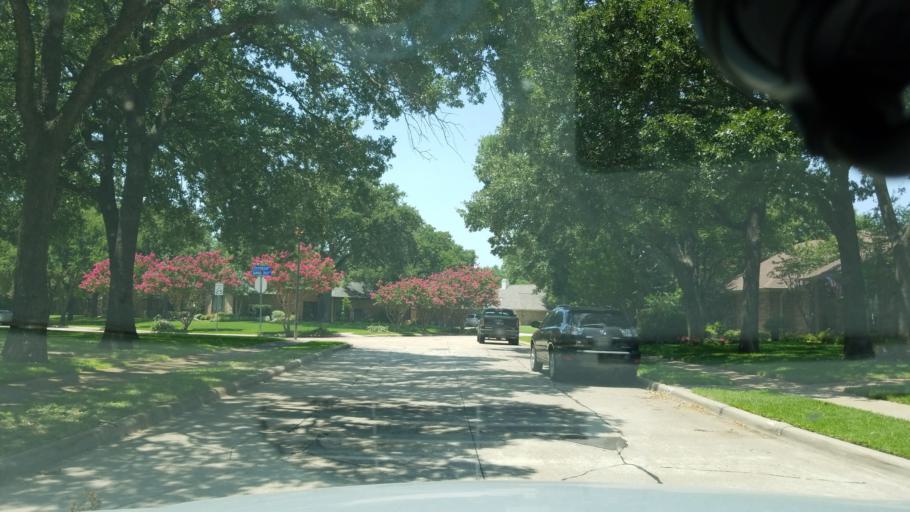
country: US
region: Texas
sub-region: Dallas County
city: Coppell
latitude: 32.9623
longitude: -96.9992
